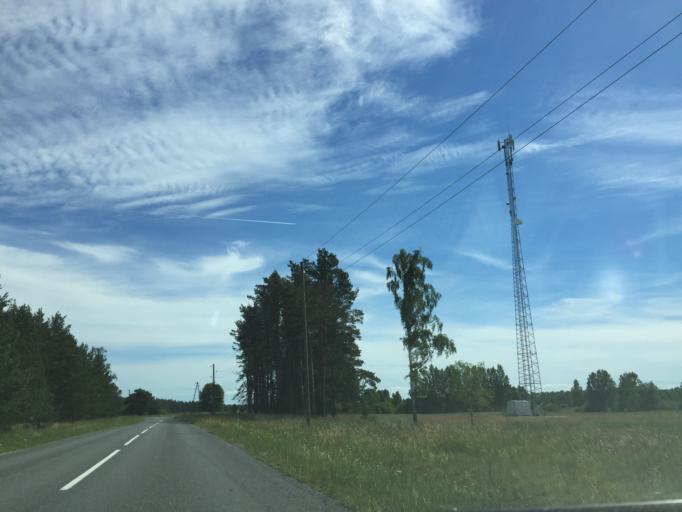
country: LV
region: Dundaga
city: Dundaga
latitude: 57.6300
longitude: 22.5720
